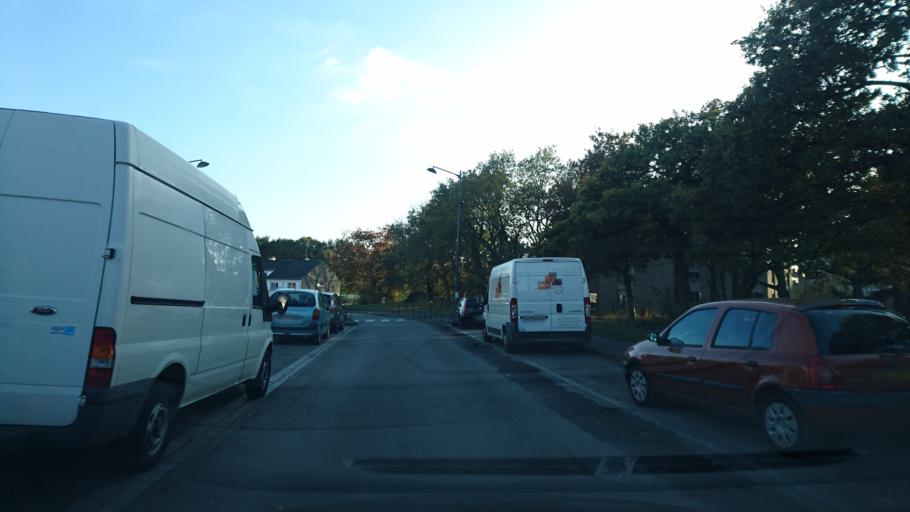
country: FR
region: Brittany
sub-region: Departement d'Ille-et-Vilaine
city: Chantepie
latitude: 48.0841
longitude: -1.6511
